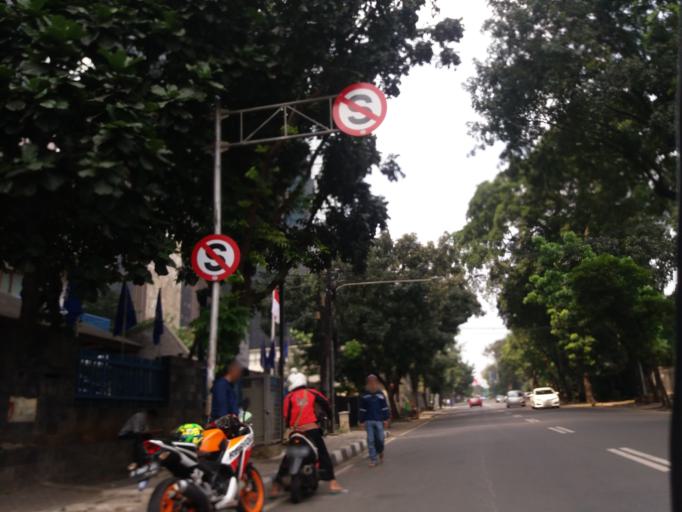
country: ID
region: Jakarta Raya
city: Jakarta
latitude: -6.2300
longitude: 106.8059
